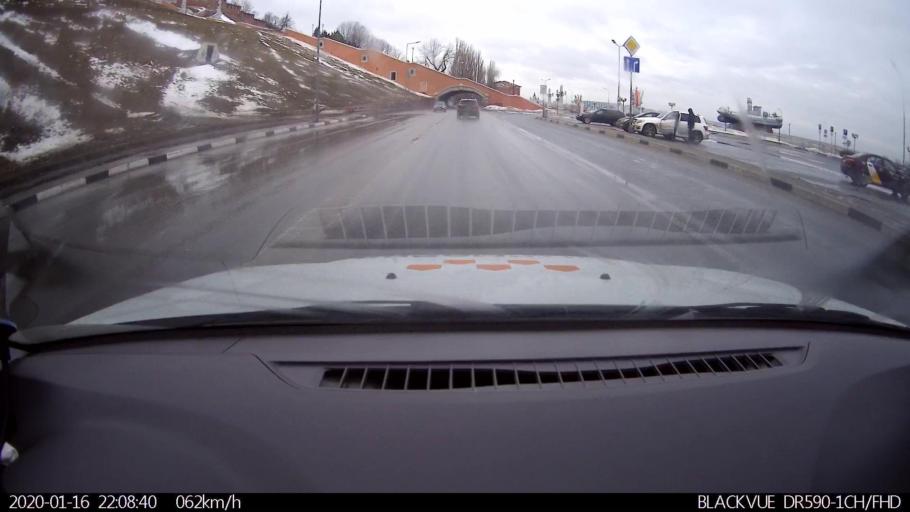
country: RU
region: Nizjnij Novgorod
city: Nizhniy Novgorod
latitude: 56.3321
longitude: 44.0109
